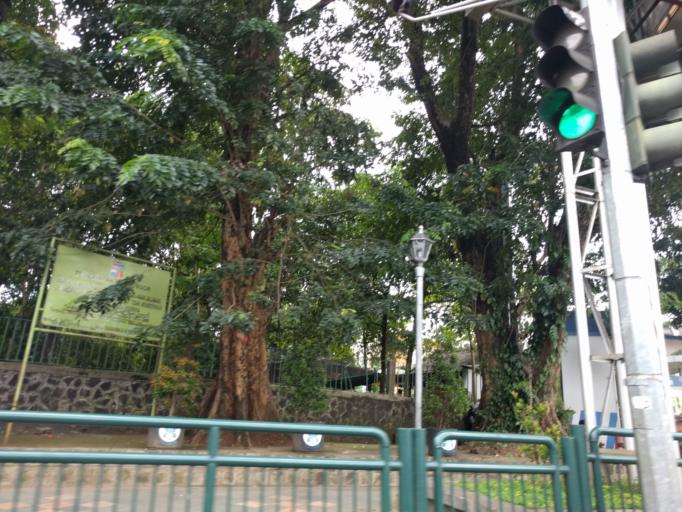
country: ID
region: West Java
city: Bogor
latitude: -6.6011
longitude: 106.8052
